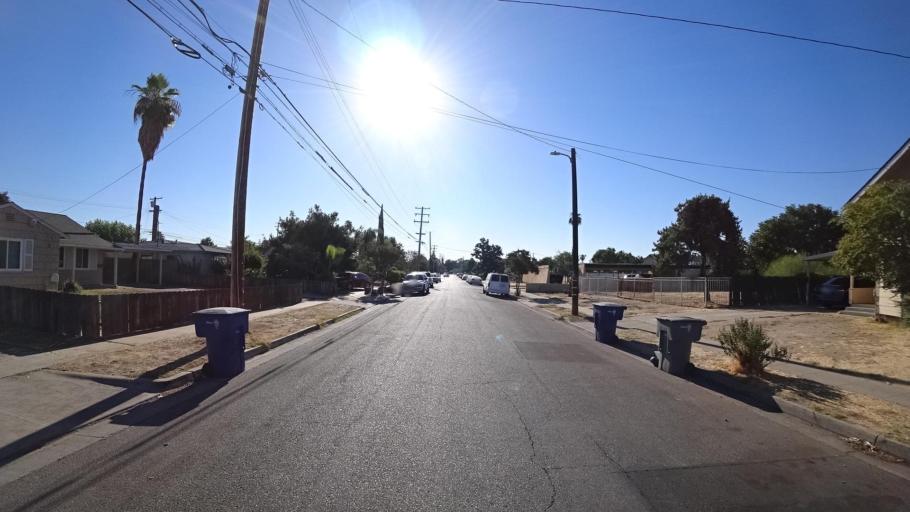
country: US
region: California
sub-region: Fresno County
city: Fresno
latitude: 36.7693
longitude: -119.8209
